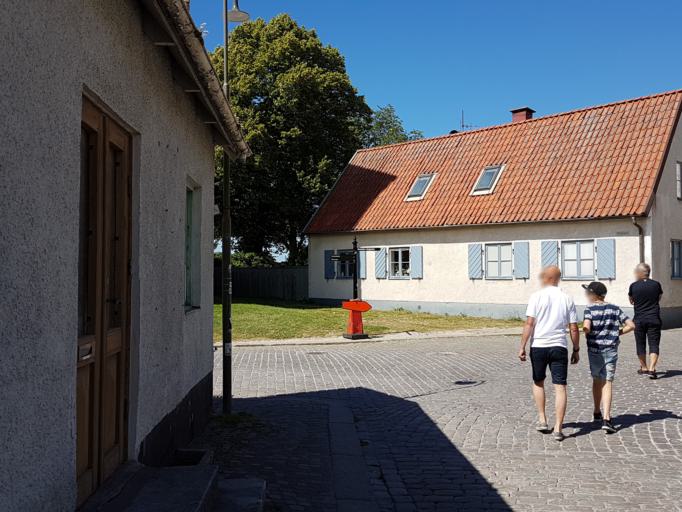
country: SE
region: Gotland
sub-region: Gotland
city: Visby
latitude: 57.6420
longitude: 18.2920
